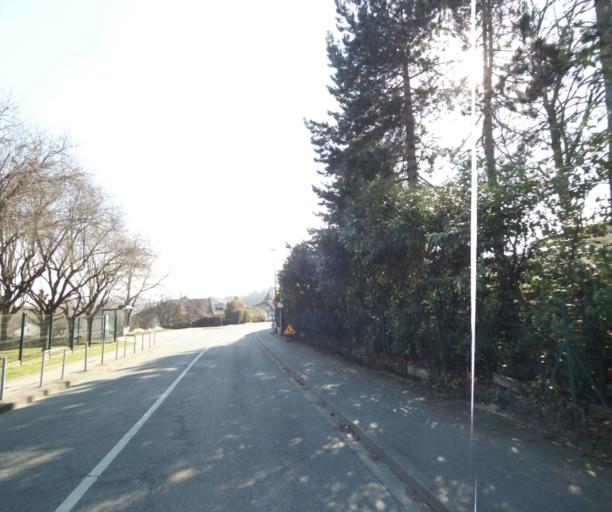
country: FR
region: Lorraine
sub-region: Departement de Meurthe-et-Moselle
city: Vandoeuvre-les-Nancy
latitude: 48.6504
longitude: 6.1763
